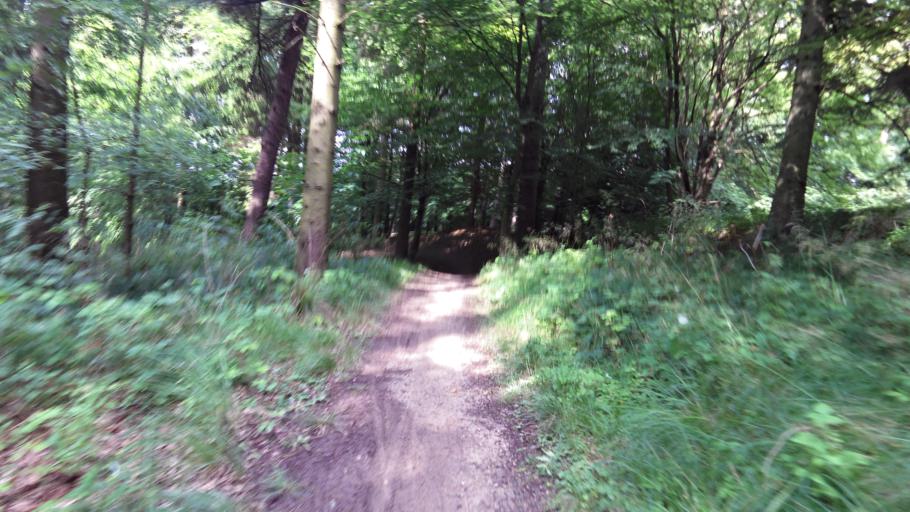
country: GB
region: England
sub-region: North Yorkshire
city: Thornton Dale
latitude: 54.2957
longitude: -0.6451
